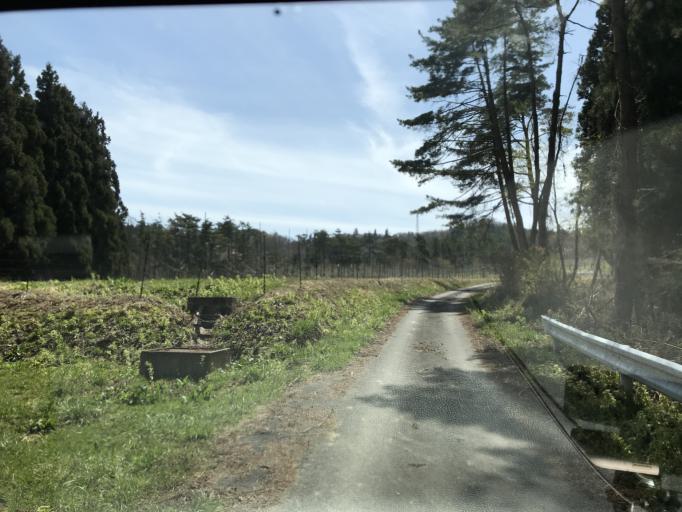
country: JP
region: Iwate
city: Ichinoseki
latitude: 38.8349
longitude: 141.2883
